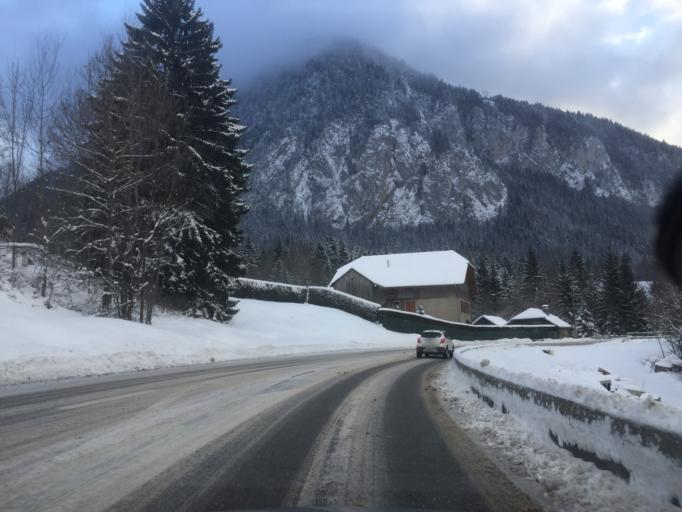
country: FR
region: Rhone-Alpes
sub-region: Departement de la Haute-Savoie
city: Abondance
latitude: 46.3124
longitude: 6.6776
